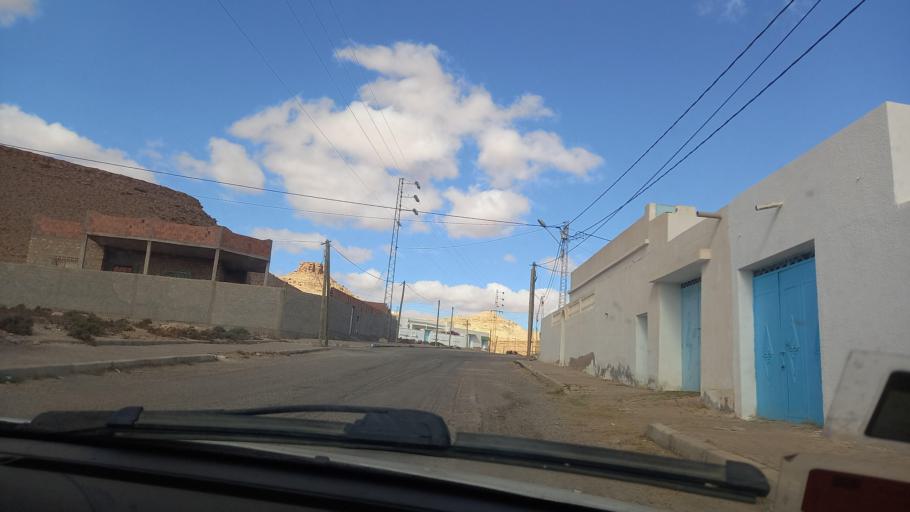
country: TN
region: Tataouine
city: Tataouine
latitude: 32.9821
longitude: 10.2644
